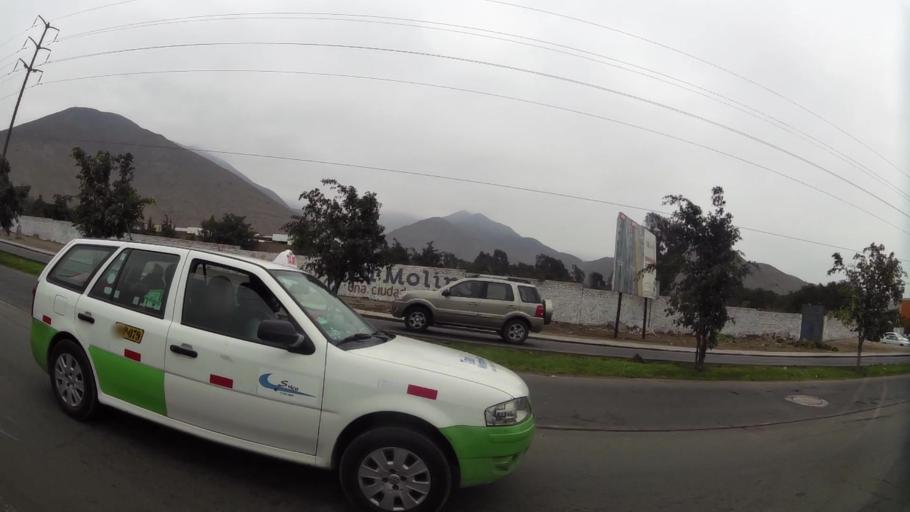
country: PE
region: Lima
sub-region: Lima
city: La Molina
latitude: -12.0850
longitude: -76.9235
